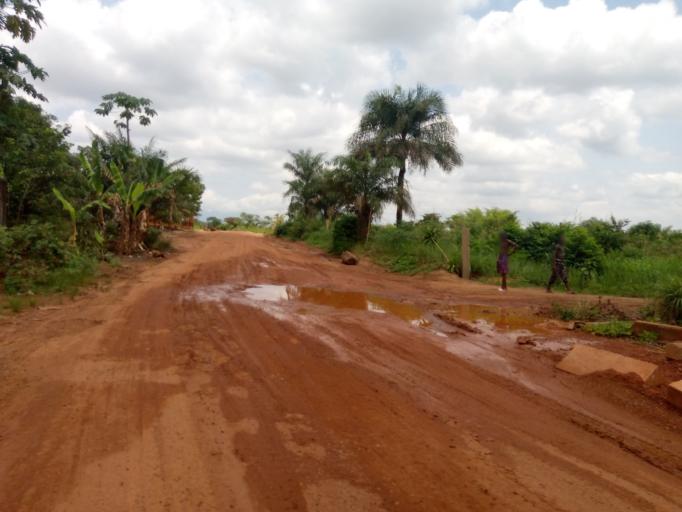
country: SL
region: Western Area
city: Waterloo
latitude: 8.3873
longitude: -12.9522
